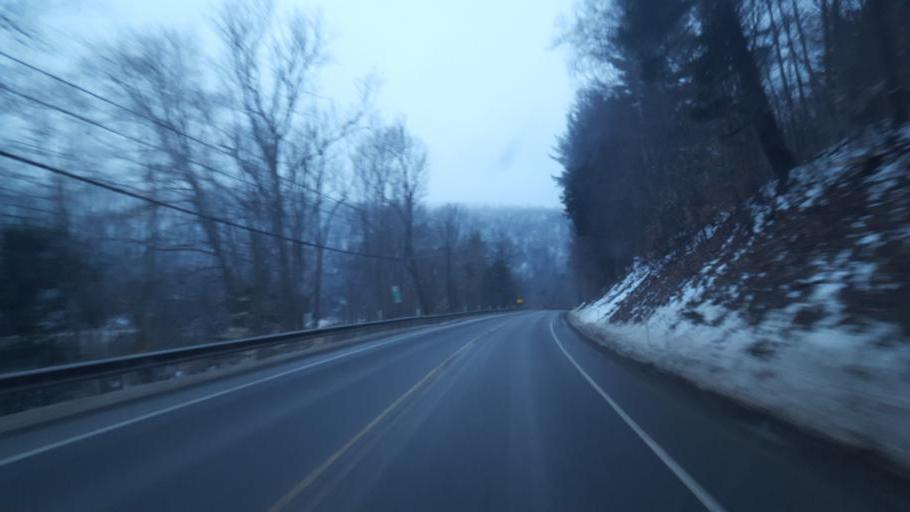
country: US
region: Pennsylvania
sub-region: Potter County
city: Coudersport
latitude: 41.7544
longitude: -78.0542
